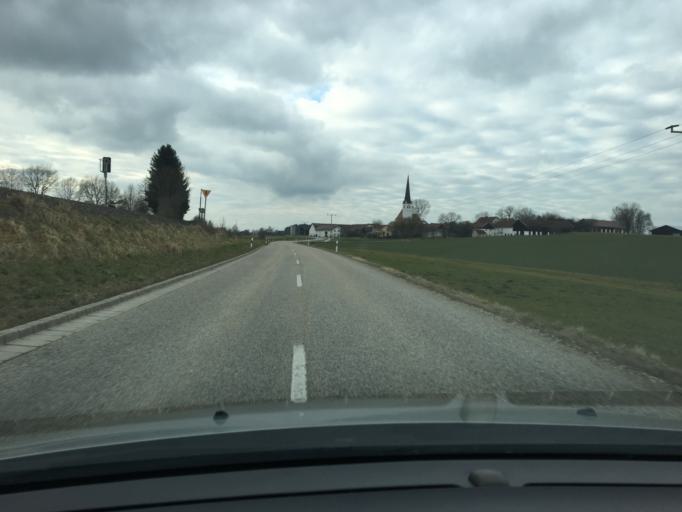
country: DE
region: Bavaria
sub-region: Lower Bavaria
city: Eging
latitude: 48.4905
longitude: 12.2156
